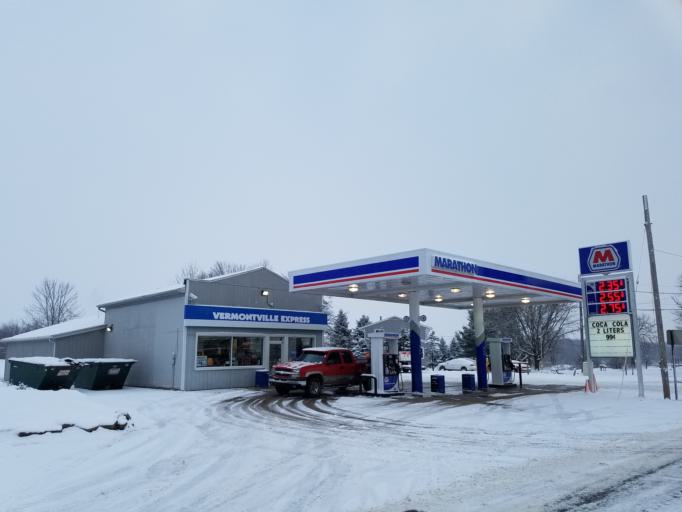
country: US
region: Michigan
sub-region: Barry County
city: Nashville
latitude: 42.6292
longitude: -85.0144
